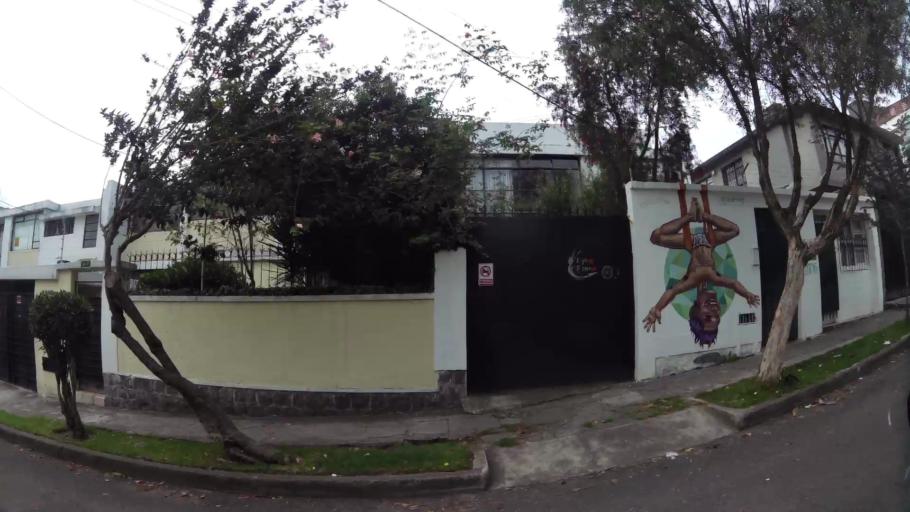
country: EC
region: Pichincha
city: Quito
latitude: -0.2077
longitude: -78.4815
